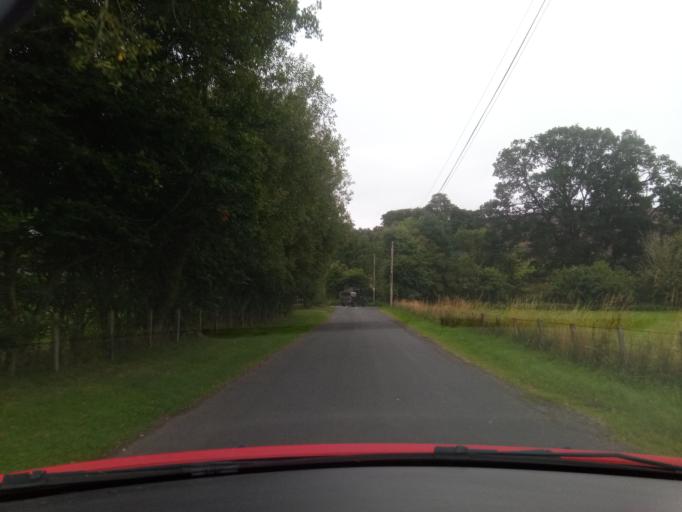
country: GB
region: England
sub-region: Northumberland
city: Rothbury
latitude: 55.2911
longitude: -2.0434
